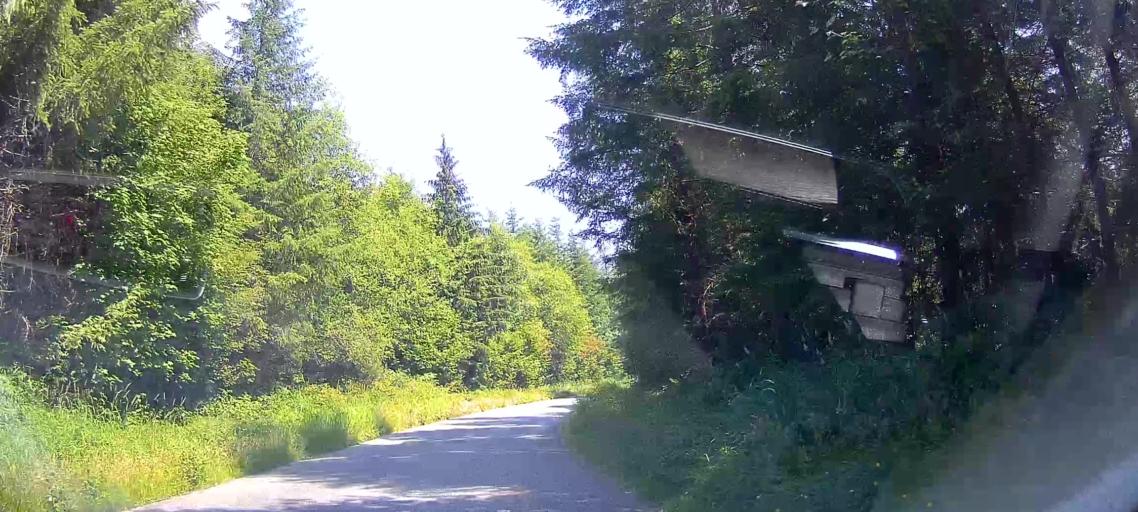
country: US
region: Washington
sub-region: Snohomish County
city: Arlington Heights
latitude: 48.3342
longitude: -122.0182
